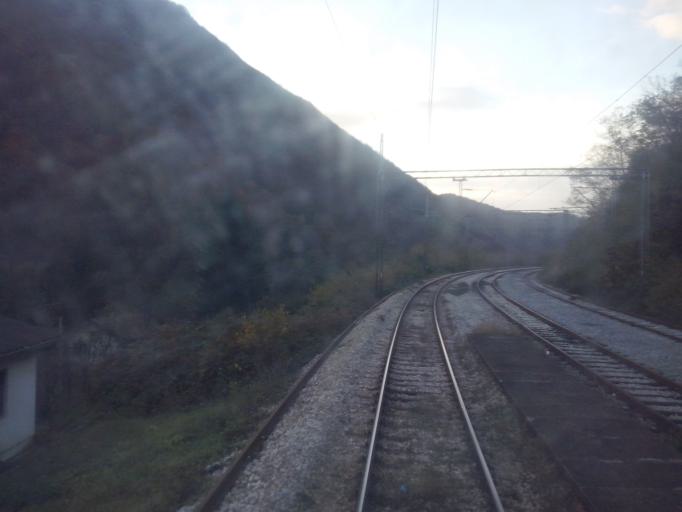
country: RS
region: Central Serbia
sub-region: Kolubarski Okrug
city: Valjevo
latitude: 44.1565
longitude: 19.8860
